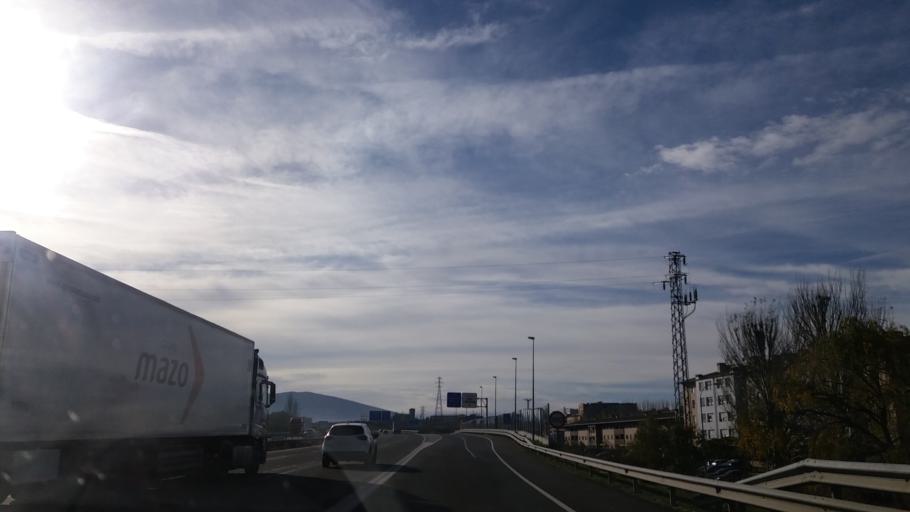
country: ES
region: Navarre
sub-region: Provincia de Navarra
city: Beriain
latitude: 42.7655
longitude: -1.6308
